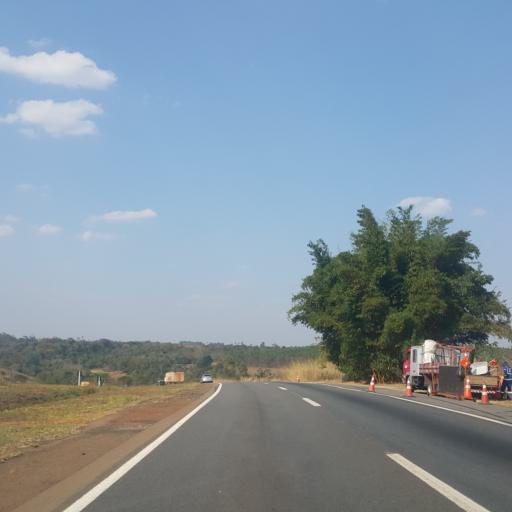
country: BR
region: Goias
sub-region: Abadiania
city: Abadiania
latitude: -16.2766
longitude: -48.7797
